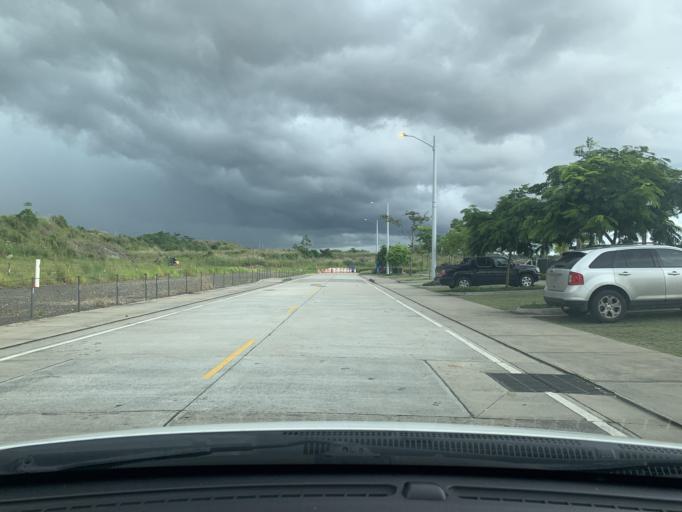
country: PA
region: Panama
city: San Miguelito
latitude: 9.0928
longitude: -79.4692
